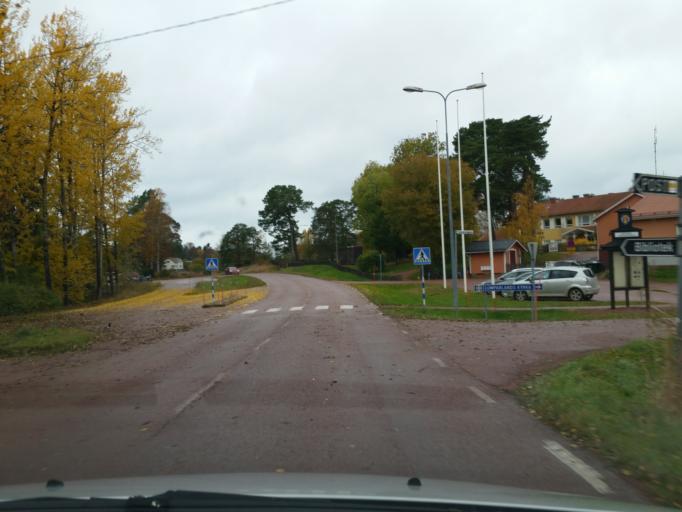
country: AX
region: Alands landsbygd
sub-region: Lumparland
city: Lumparland
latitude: 60.1166
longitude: 20.2592
